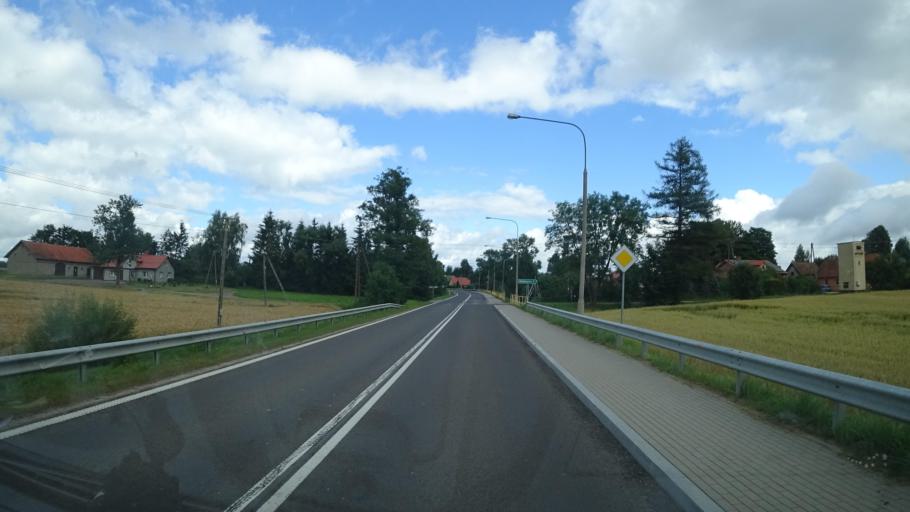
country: PL
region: Warmian-Masurian Voivodeship
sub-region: Powiat olecki
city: Kowale Oleckie
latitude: 54.2067
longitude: 22.4121
